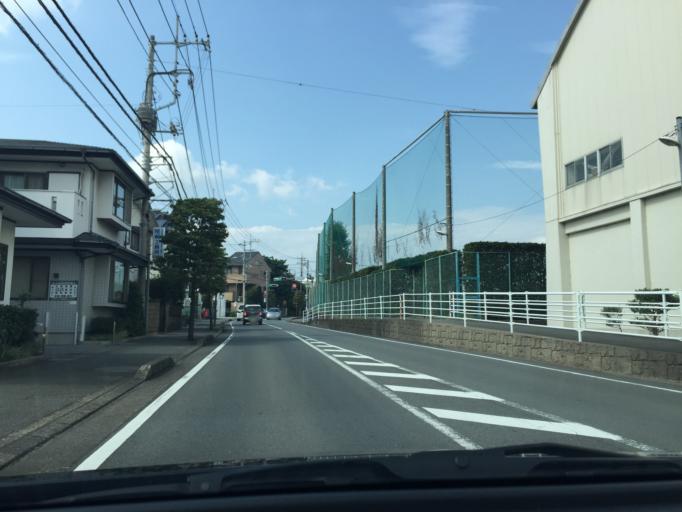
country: JP
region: Shizuoka
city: Mishima
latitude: 35.1325
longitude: 138.8984
